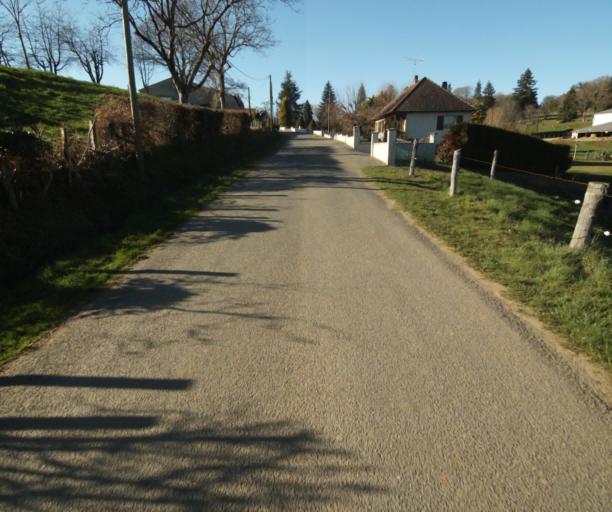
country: FR
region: Limousin
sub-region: Departement de la Correze
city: Seilhac
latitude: 45.3775
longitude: 1.7158
